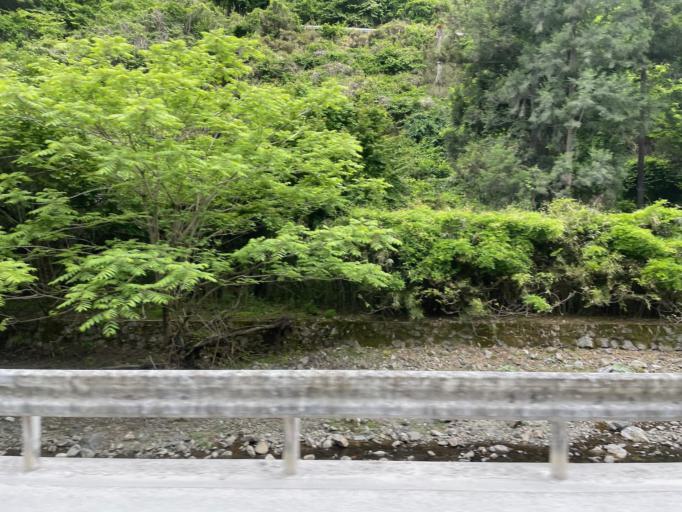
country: JP
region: Tochigi
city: Tanuma
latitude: 36.4560
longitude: 139.6079
